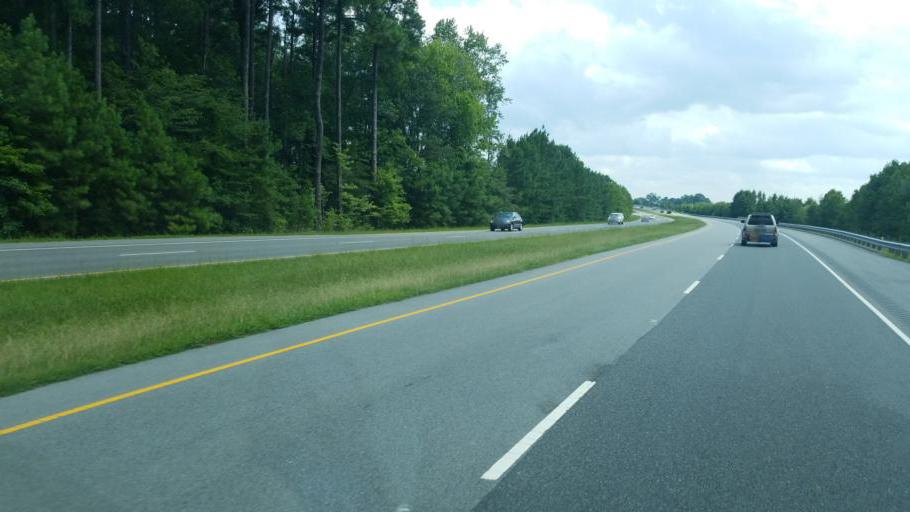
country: US
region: North Carolina
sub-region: Currituck County
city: Moyock
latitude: 36.6246
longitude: -76.2147
